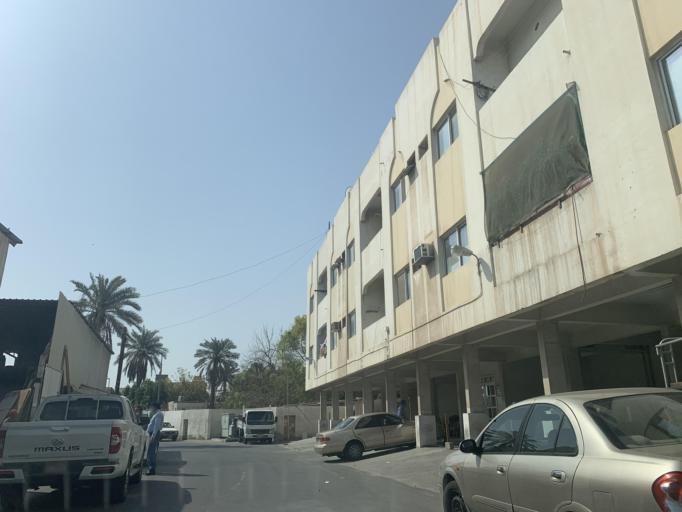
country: BH
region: Manama
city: Manama
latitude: 26.2242
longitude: 50.5663
